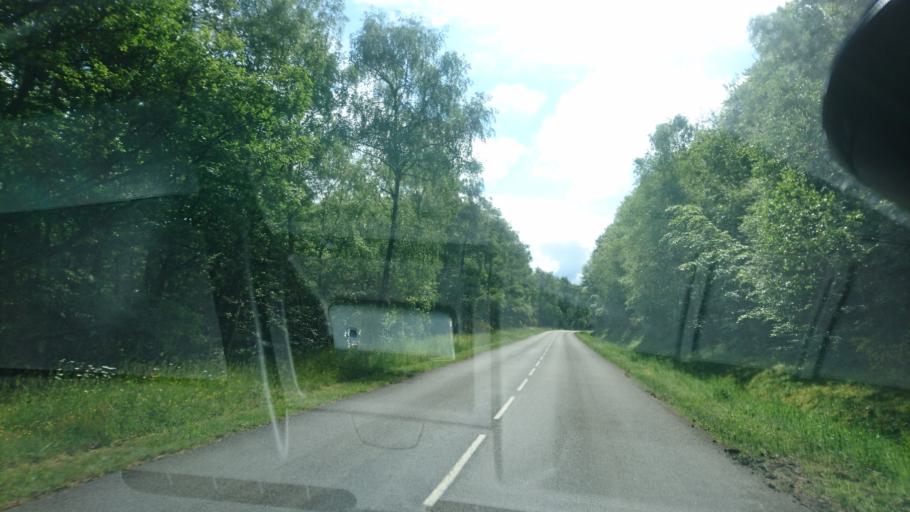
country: FR
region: Limousin
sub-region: Departement de la Haute-Vienne
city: Peyrat-le-Chateau
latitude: 45.7957
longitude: 1.8457
